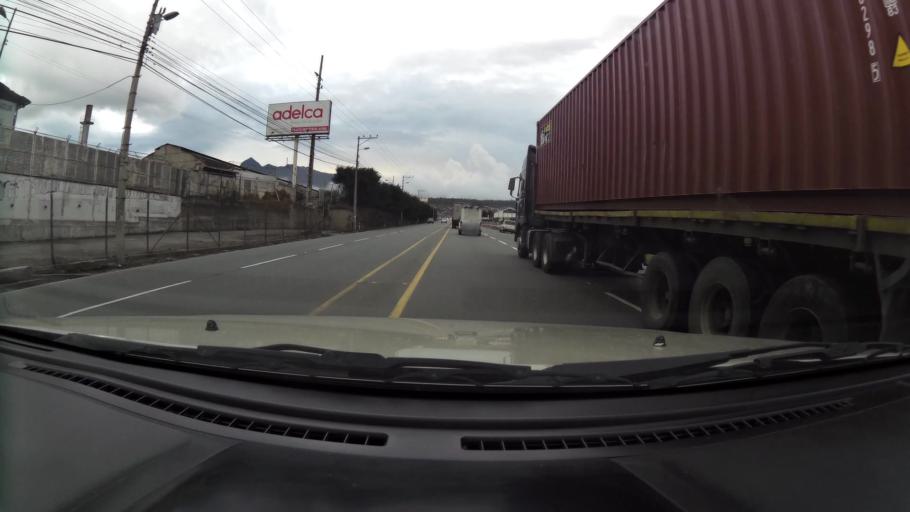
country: EC
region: Pichincha
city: Machachi
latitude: -0.4459
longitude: -78.6321
